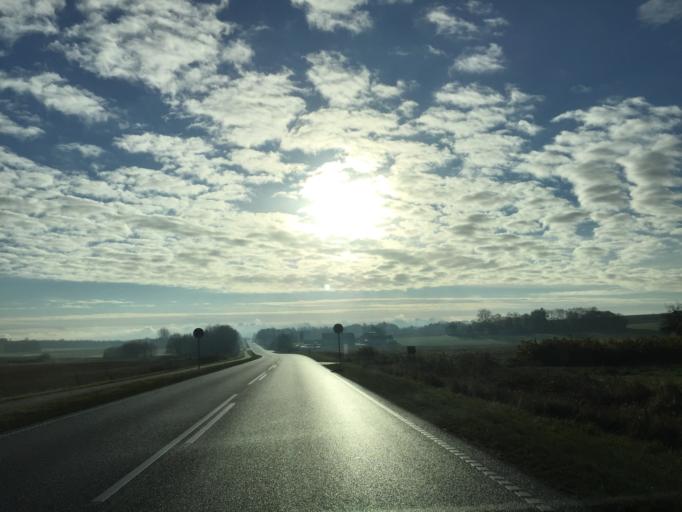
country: DK
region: Central Jutland
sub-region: Arhus Kommune
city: Sabro
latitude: 56.2077
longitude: 10.0190
